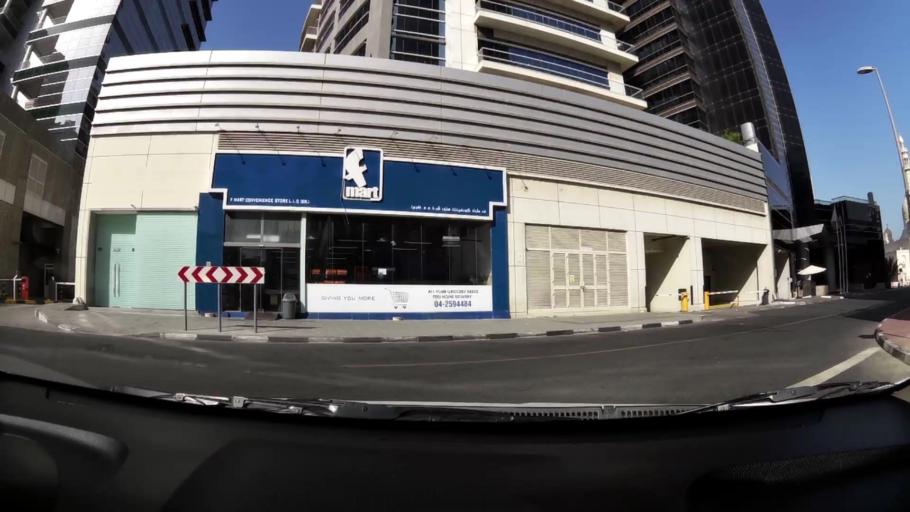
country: AE
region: Ash Shariqah
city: Sharjah
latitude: 25.2600
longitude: 55.3192
